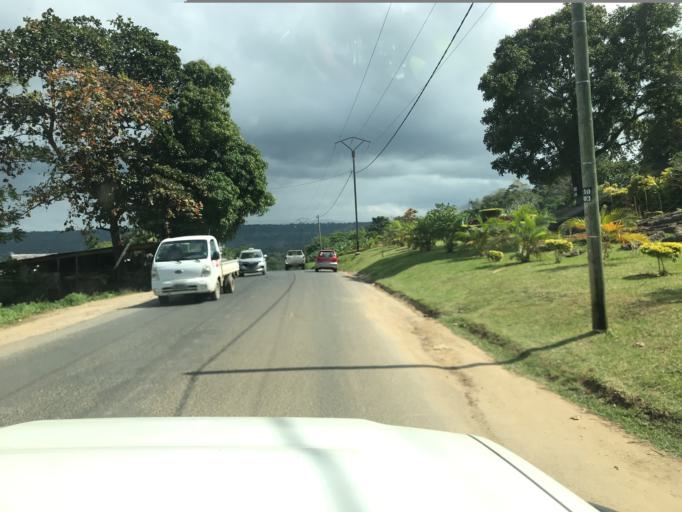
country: VU
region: Sanma
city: Luganville
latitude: -15.5103
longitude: 167.1826
